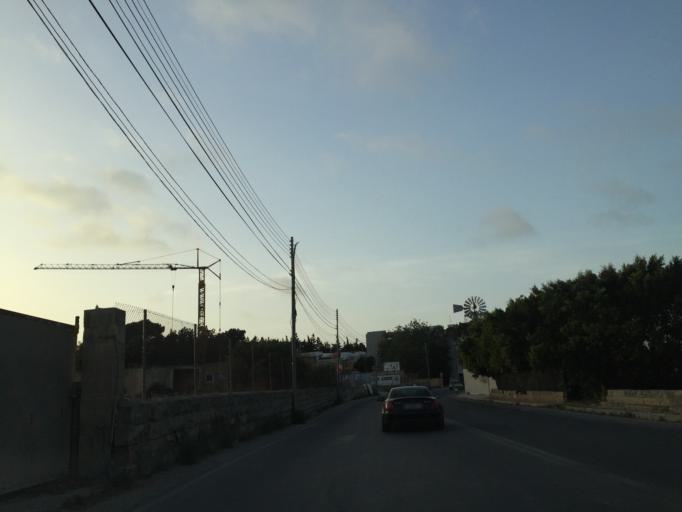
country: MT
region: Saint Paul's Bay
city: San Pawl il-Bahar
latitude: 35.9383
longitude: 14.4114
